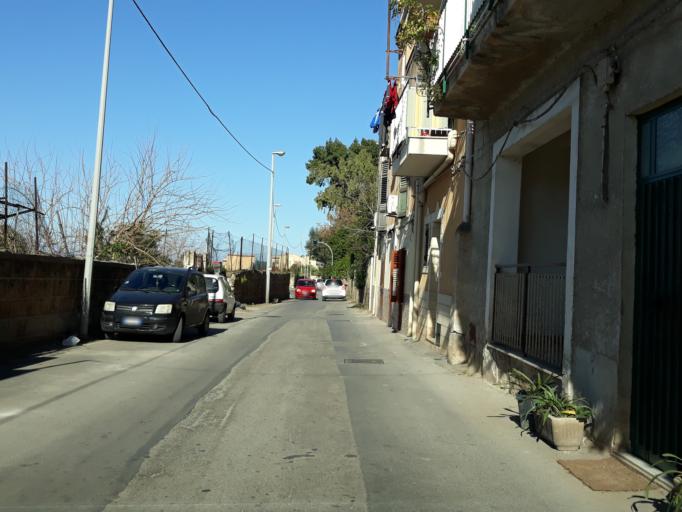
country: IT
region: Sicily
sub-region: Palermo
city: Ciaculli
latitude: 38.0816
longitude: 13.3747
